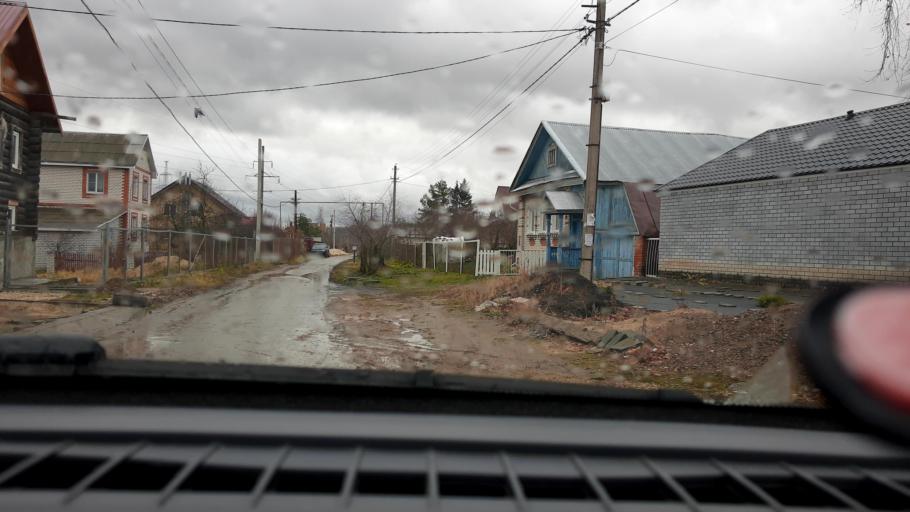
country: RU
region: Nizjnij Novgorod
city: Afonino
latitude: 56.2710
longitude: 44.1073
